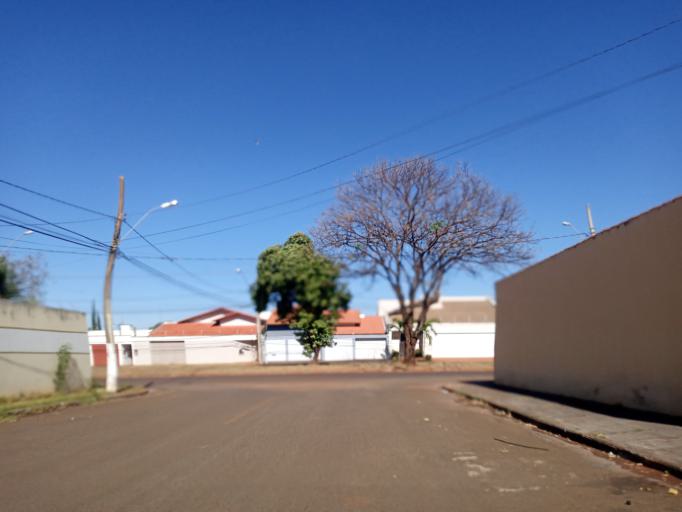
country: BR
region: Minas Gerais
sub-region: Ituiutaba
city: Ituiutaba
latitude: -18.9685
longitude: -49.4495
